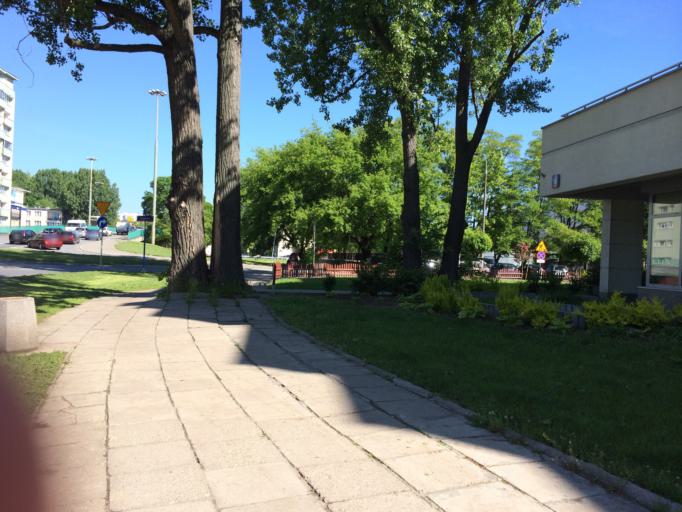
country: PL
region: Masovian Voivodeship
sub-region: Warszawa
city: Praga Poludnie
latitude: 52.2272
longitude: 21.0644
